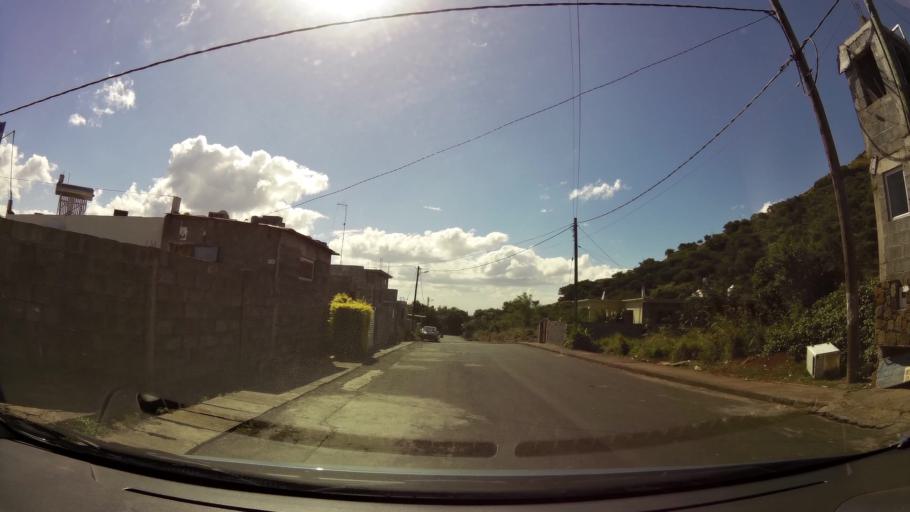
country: MU
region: Black River
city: Cascavelle
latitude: -20.2659
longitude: 57.4212
